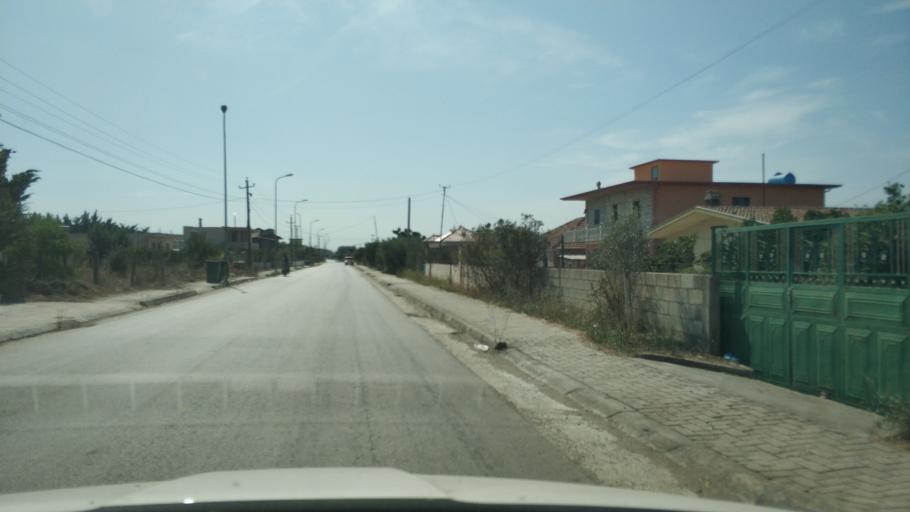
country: AL
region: Fier
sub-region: Rrethi i Lushnjes
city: Divjake
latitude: 40.9739
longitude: 19.5357
